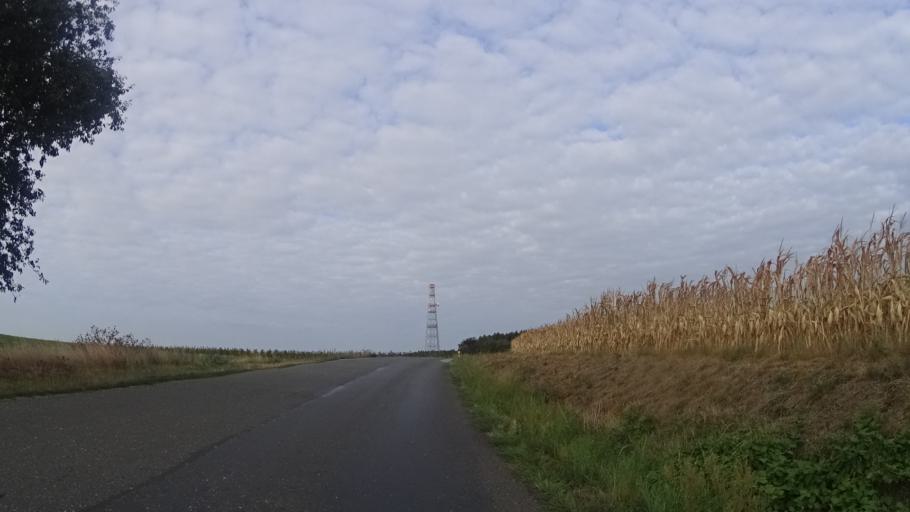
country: CZ
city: Stezery
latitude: 50.2119
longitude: 15.7334
